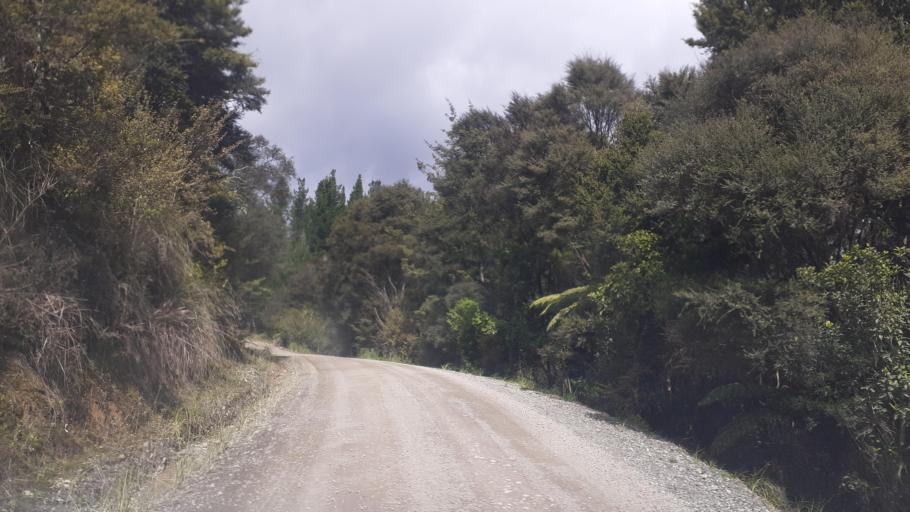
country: NZ
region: Northland
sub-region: Far North District
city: Moerewa
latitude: -35.5794
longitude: 173.9424
